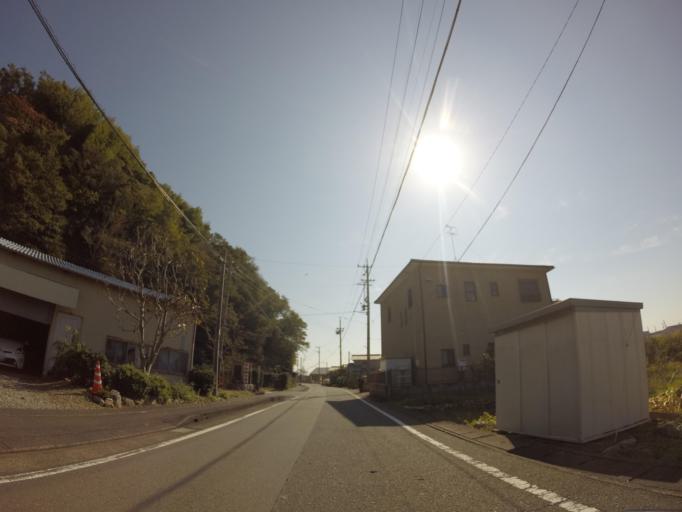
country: JP
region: Shizuoka
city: Shizuoka-shi
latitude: 35.0616
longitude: 138.5324
